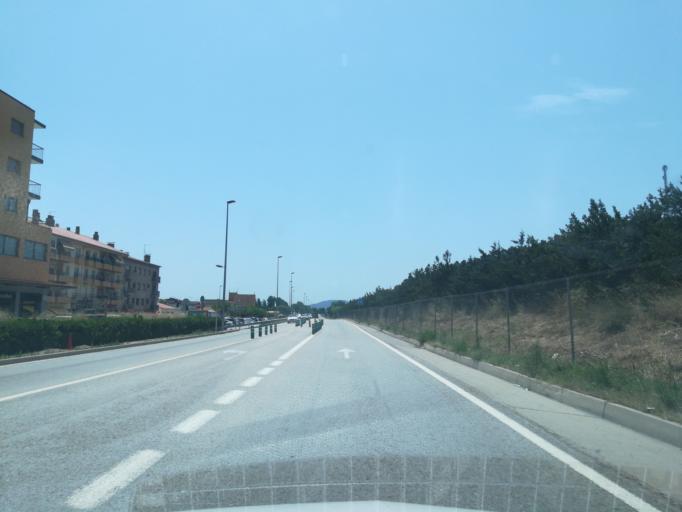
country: ES
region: Catalonia
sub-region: Provincia de Girona
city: la Jonquera
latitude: 42.4203
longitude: 2.8708
